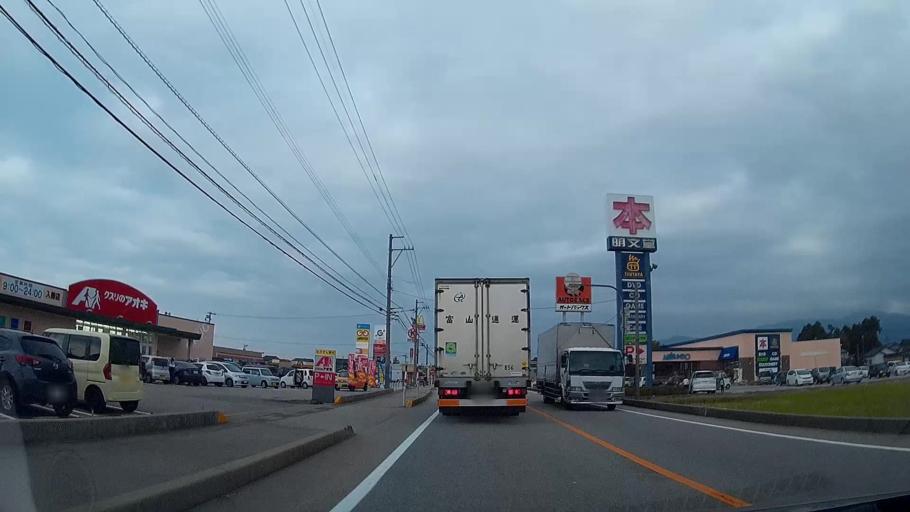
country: JP
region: Toyama
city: Nyuzen
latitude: 36.9397
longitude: 137.5144
